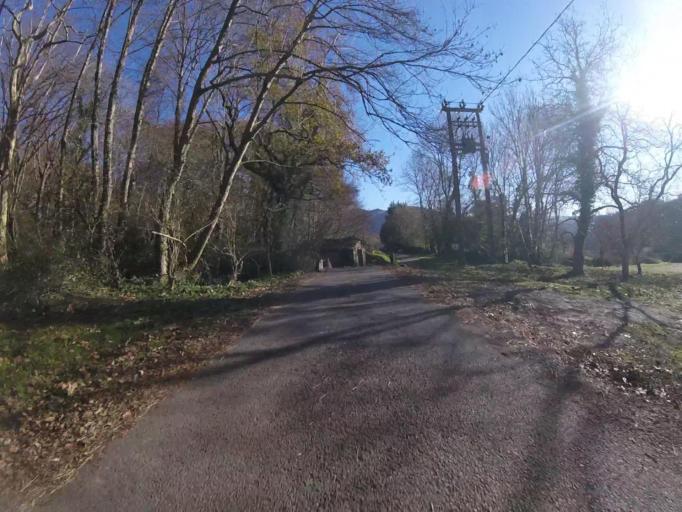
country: ES
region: Navarre
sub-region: Provincia de Navarra
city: Bera
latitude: 43.2946
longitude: -1.6487
